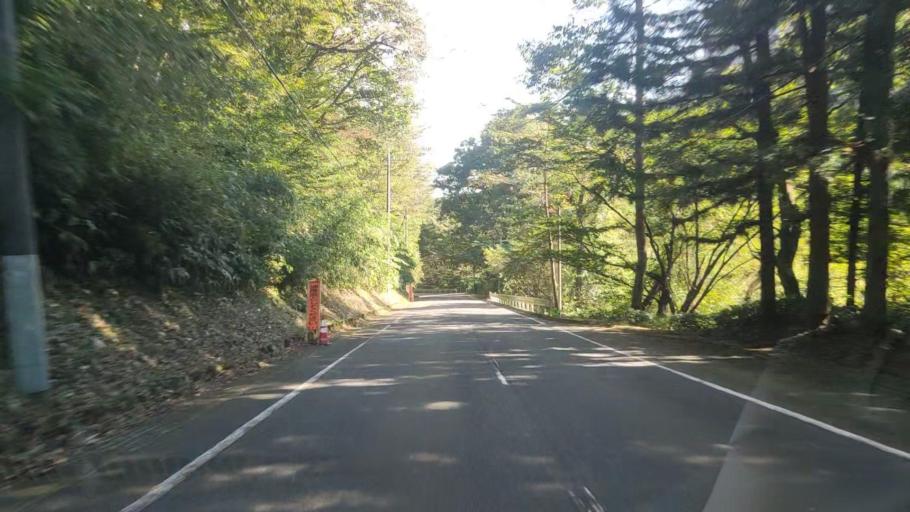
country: JP
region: Gunma
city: Nakanojomachi
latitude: 36.6125
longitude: 138.7393
